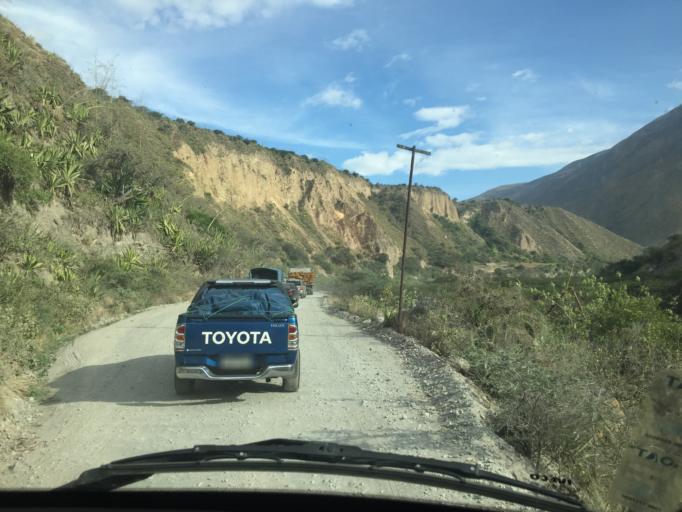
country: EC
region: Carchi
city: El Angel
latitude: 0.5993
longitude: -78.1379
